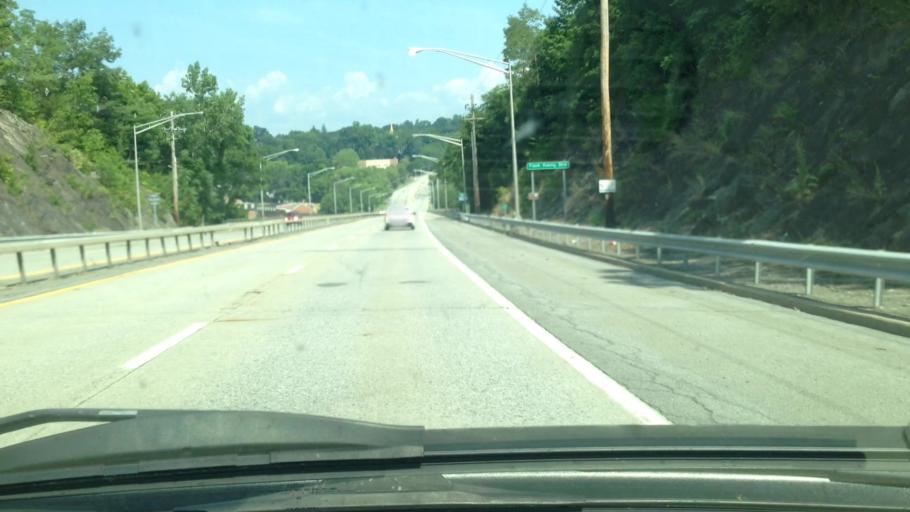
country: US
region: New York
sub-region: Ulster County
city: Port Ewen
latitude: 41.9157
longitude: -73.9802
